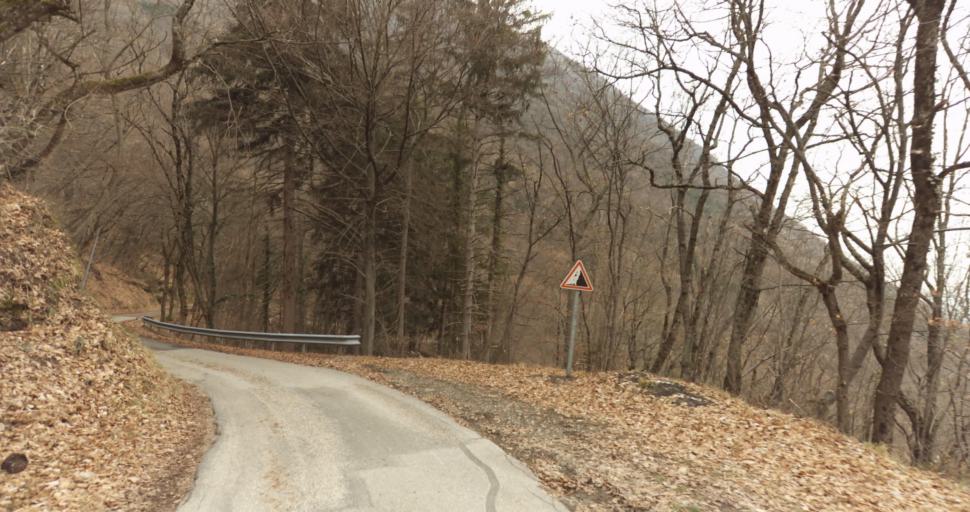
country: FR
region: Rhone-Alpes
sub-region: Departement de l'Isere
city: Saint-Georges-de-Commiers
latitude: 45.0260
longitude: 5.6886
